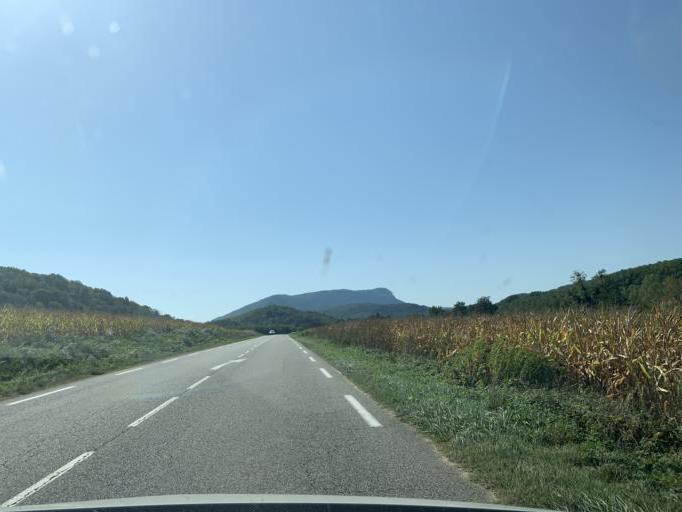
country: FR
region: Rhone-Alpes
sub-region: Departement de l'Ain
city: Belley
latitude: 45.7240
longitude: 5.6654
